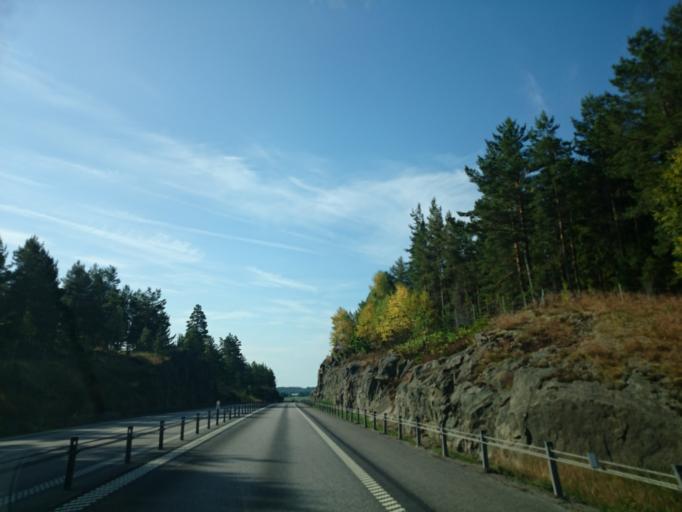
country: SE
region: OEstergoetland
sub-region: Valdemarsviks Kommun
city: Gusum
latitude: 58.3445
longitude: 16.4489
